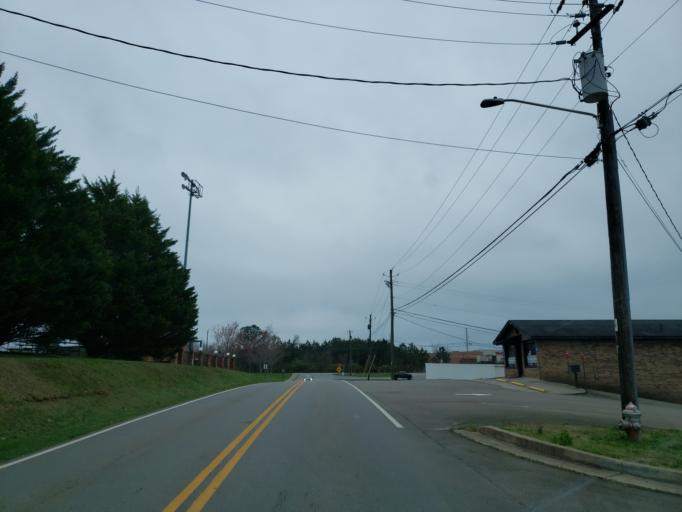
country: US
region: Georgia
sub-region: Pickens County
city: Jasper
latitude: 34.4710
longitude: -84.4276
